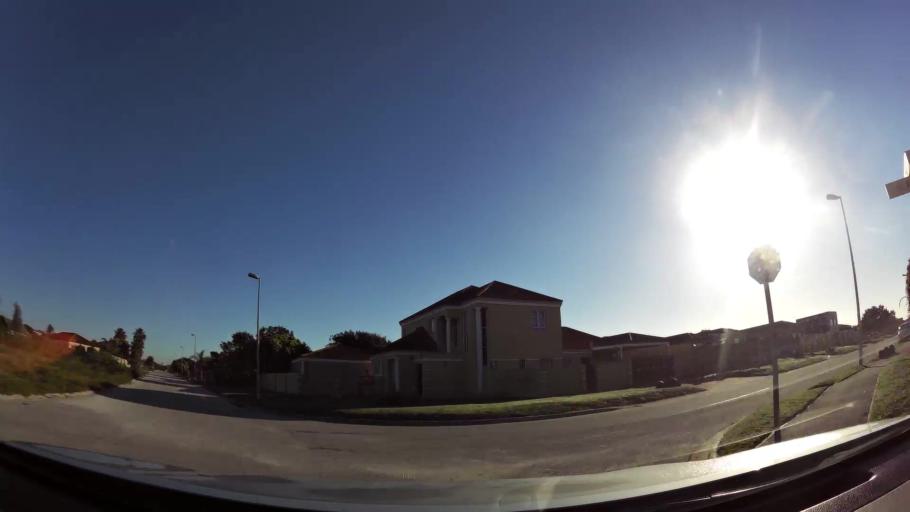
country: ZA
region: Eastern Cape
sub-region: Nelson Mandela Bay Metropolitan Municipality
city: Port Elizabeth
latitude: -34.0028
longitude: 25.6512
